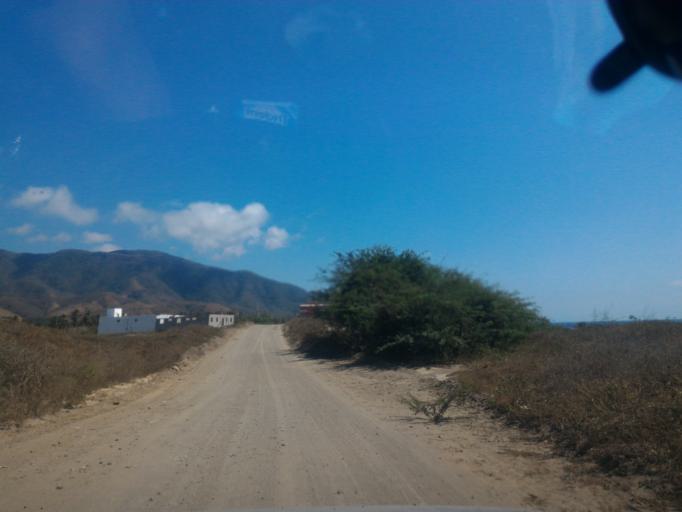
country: MX
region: Michoacan
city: Coahuayana Viejo
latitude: 18.5896
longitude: -103.6849
